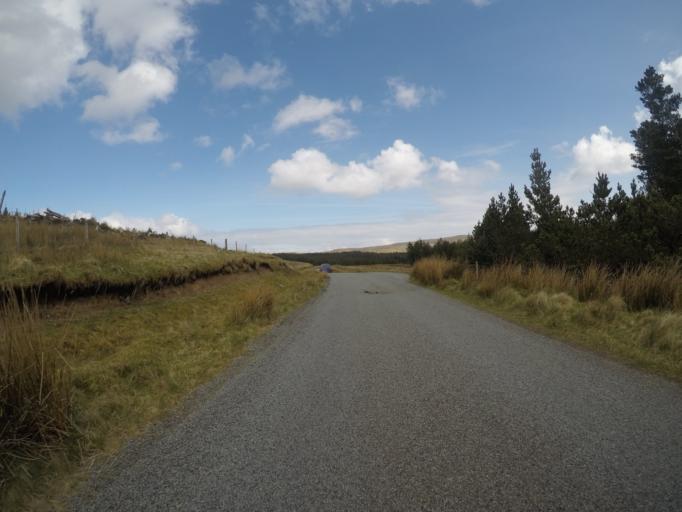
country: GB
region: Scotland
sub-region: Highland
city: Isle of Skye
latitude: 57.4070
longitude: -6.3204
